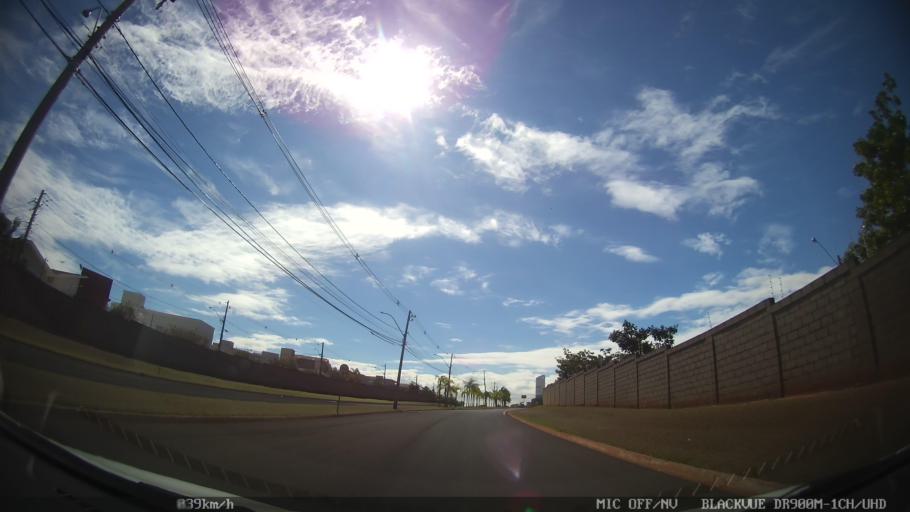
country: BR
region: Sao Paulo
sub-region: Bady Bassitt
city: Bady Bassitt
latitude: -20.8252
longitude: -49.4826
